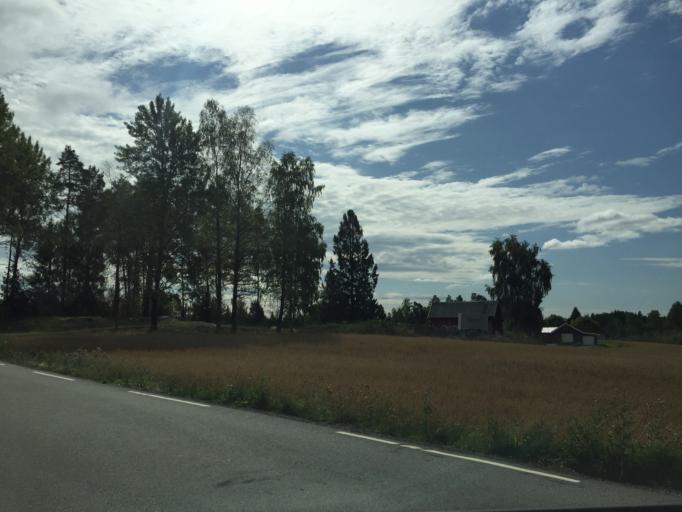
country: NO
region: Akershus
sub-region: Ski
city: Ski
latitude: 59.6510
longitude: 10.8728
